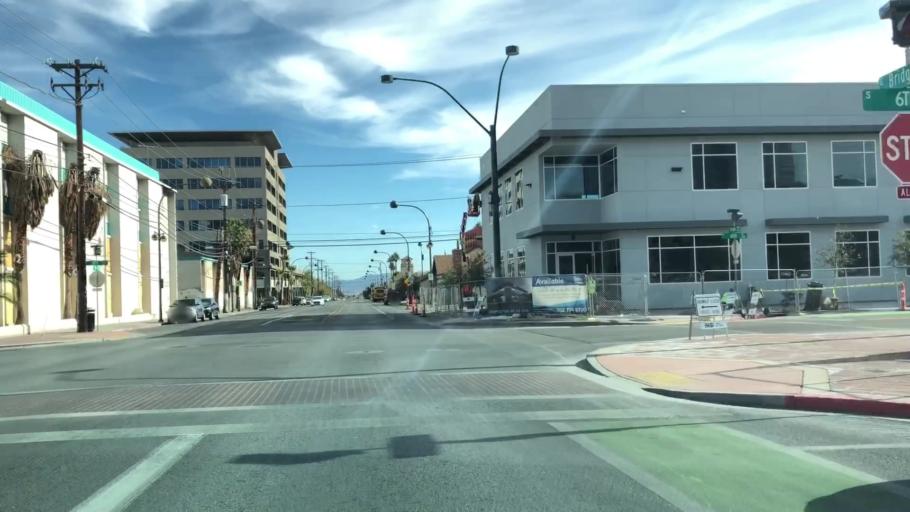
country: US
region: Nevada
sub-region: Clark County
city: Las Vegas
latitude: 36.1665
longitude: -115.1413
